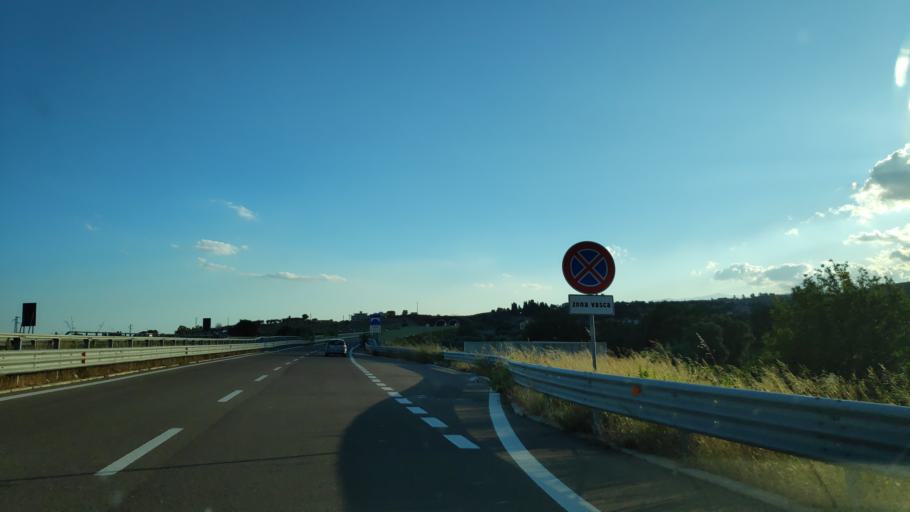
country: IT
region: Calabria
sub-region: Provincia di Reggio Calabria
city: Locri
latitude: 38.2505
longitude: 16.2573
